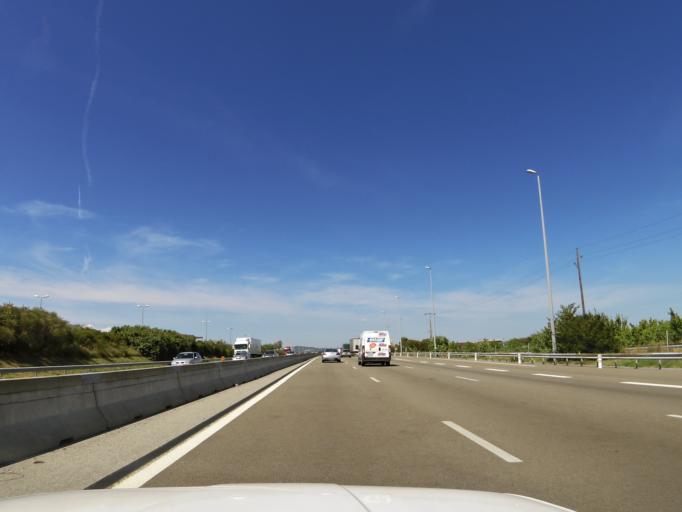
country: FR
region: Rhone-Alpes
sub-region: Departement de la Drome
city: La Roche-de-Glun
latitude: 45.0167
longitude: 4.8759
